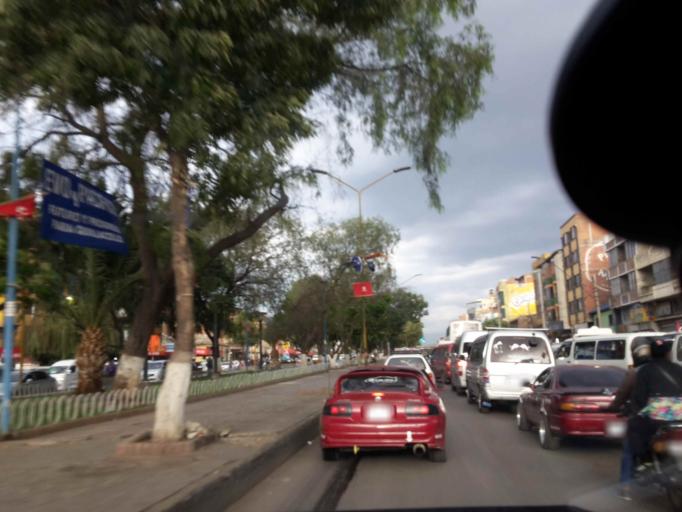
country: BO
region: Cochabamba
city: Sipe Sipe
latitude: -17.3942
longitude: -66.2805
